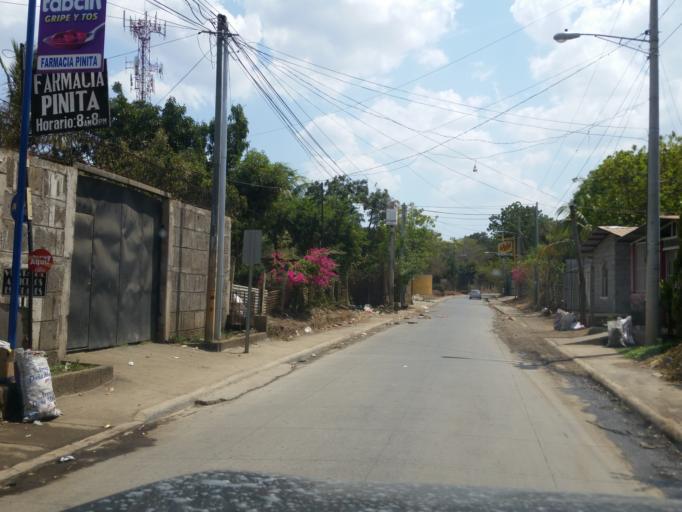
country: NI
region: Masaya
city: Ticuantepe
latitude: 12.0729
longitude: -86.1973
